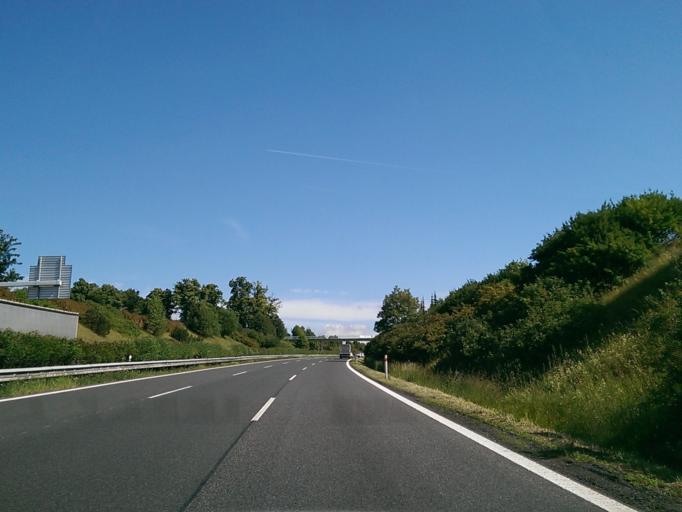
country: CZ
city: Ohrazenice
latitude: 50.6243
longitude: 15.1085
